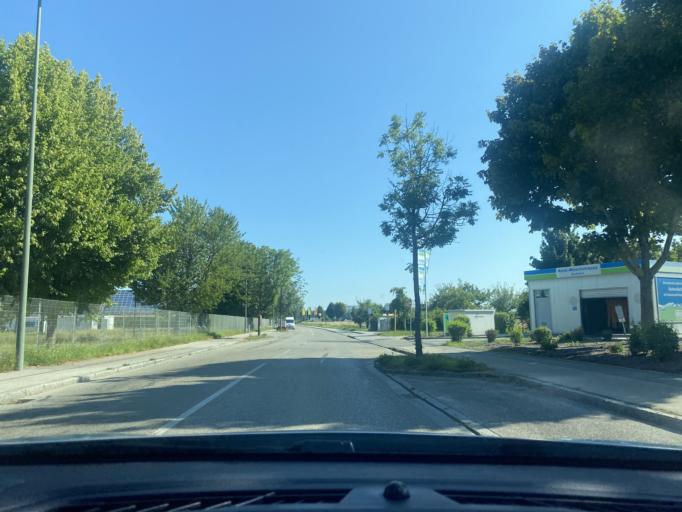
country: DE
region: Bavaria
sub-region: Upper Bavaria
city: Erding
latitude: 48.2766
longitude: 11.8987
